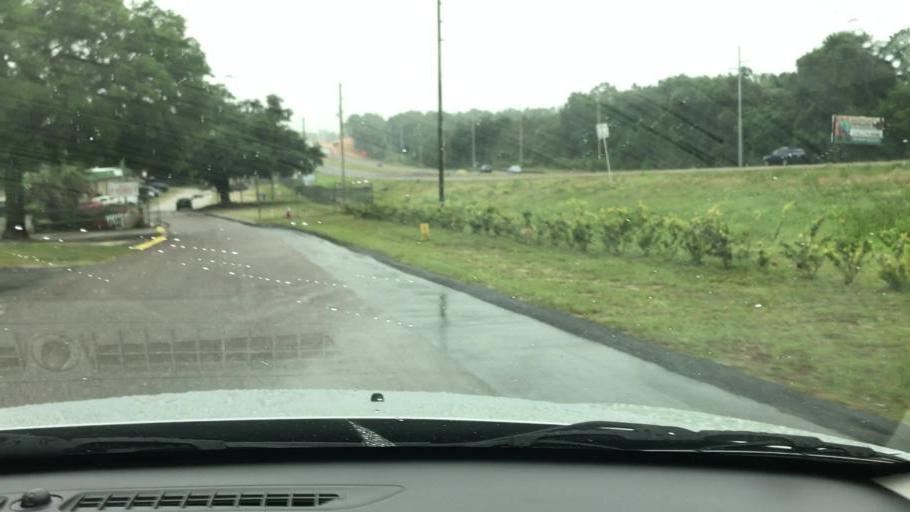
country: US
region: Florida
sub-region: Lake County
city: Mount Dora
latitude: 28.8064
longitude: -81.6249
